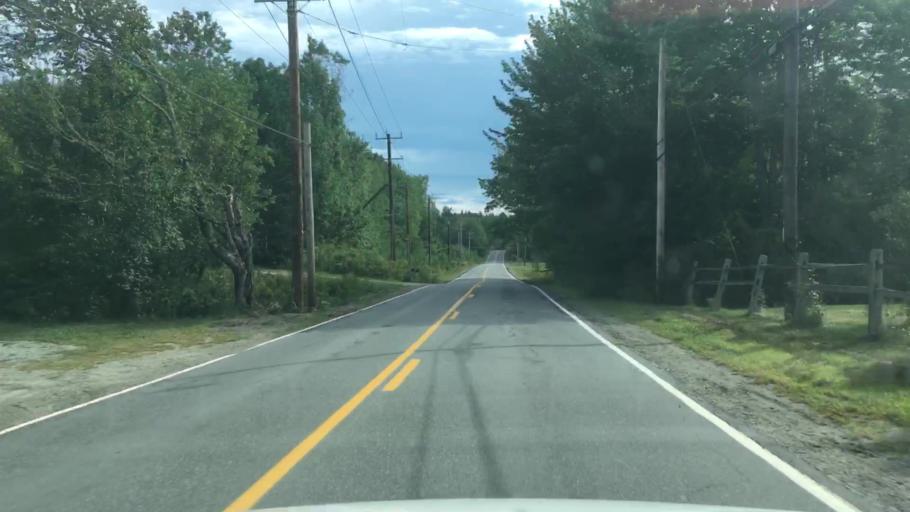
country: US
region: Maine
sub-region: Hancock County
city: Ellsworth
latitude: 44.4871
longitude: -68.4201
